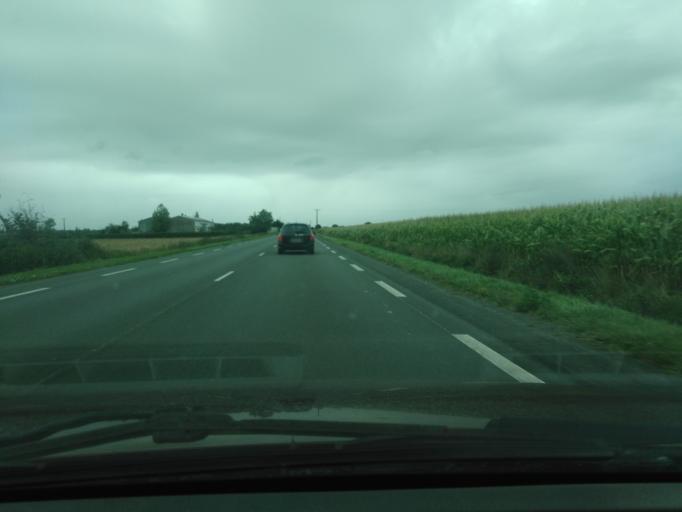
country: FR
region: Pays de la Loire
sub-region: Departement de la Vendee
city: Sainte-Gemme-la-Plaine
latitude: 46.4558
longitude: -1.1052
